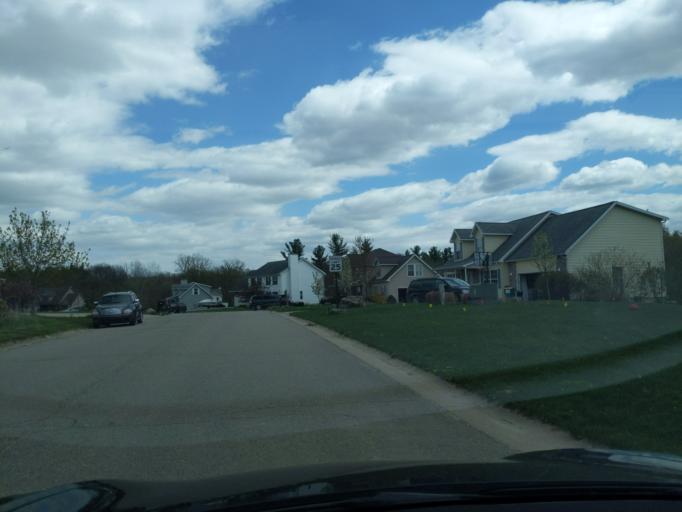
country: US
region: Michigan
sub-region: Eaton County
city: Dimondale
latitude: 42.6357
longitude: -84.6126
